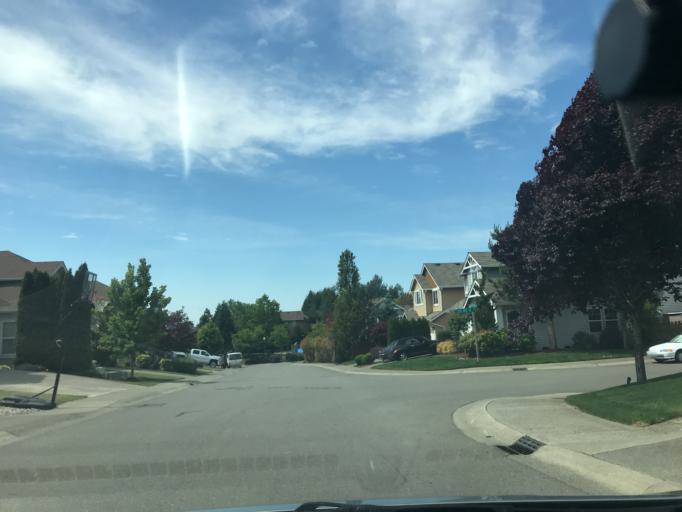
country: US
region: Washington
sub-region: King County
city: Ravensdale
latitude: 47.3511
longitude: -122.0073
